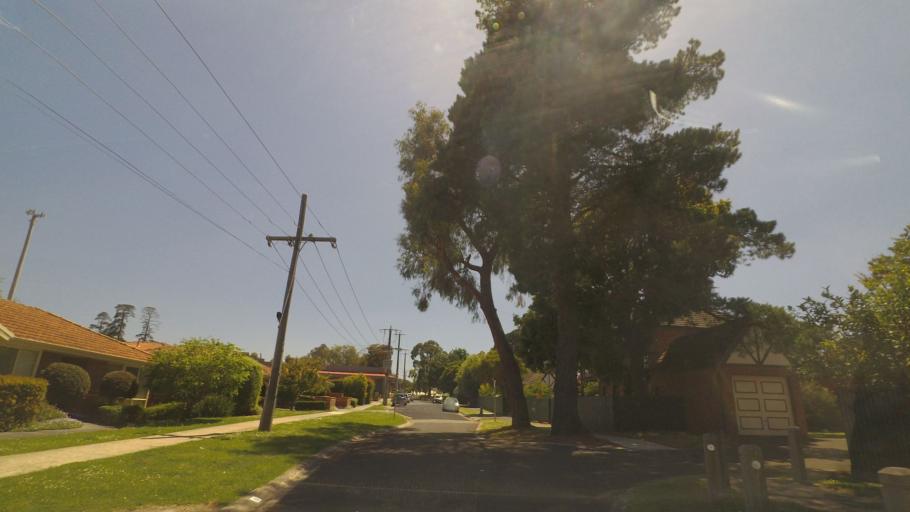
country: AU
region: Victoria
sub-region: Yarra Ranges
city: Montrose
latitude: -37.8118
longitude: 145.3436
